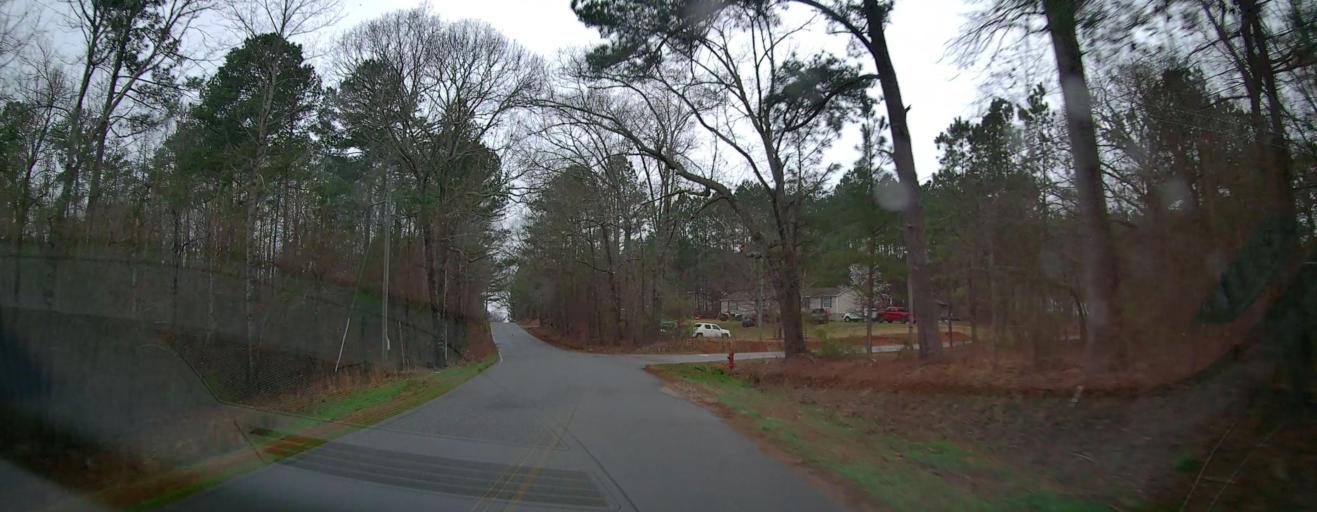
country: US
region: Georgia
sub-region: Monroe County
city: Forsyth
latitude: 33.0872
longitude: -83.9298
